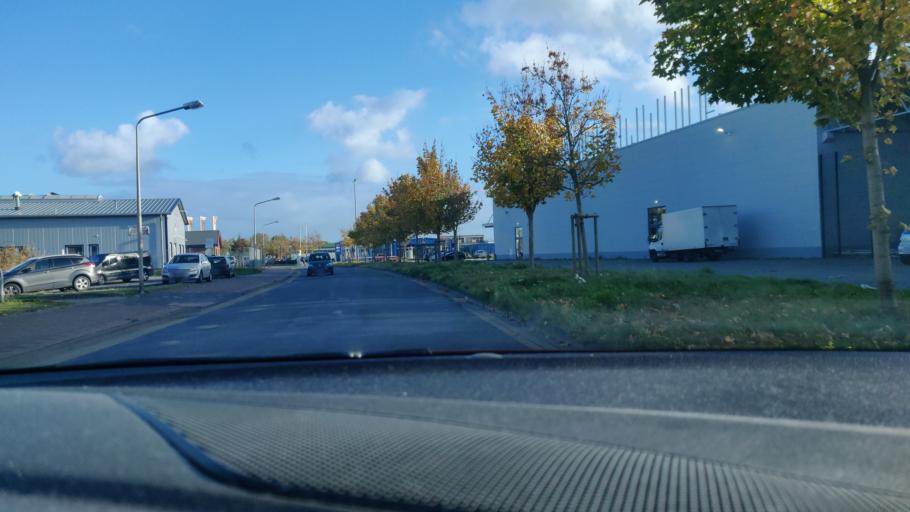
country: DE
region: Lower Saxony
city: Cuxhaven
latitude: 53.8554
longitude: 8.7119
